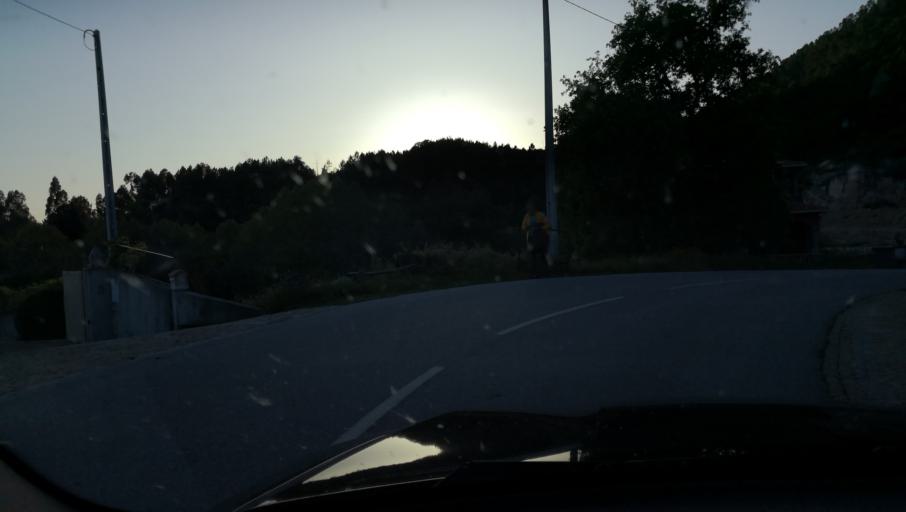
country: PT
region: Vila Real
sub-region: Mondim de Basto
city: Mondim de Basto
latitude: 41.4060
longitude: -7.9128
